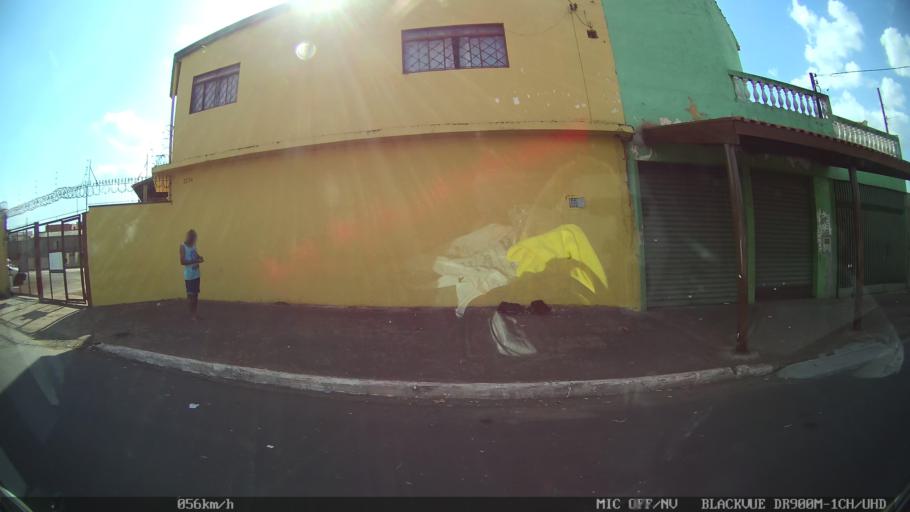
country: BR
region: Sao Paulo
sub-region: Ribeirao Preto
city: Ribeirao Preto
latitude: -21.2029
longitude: -47.8505
